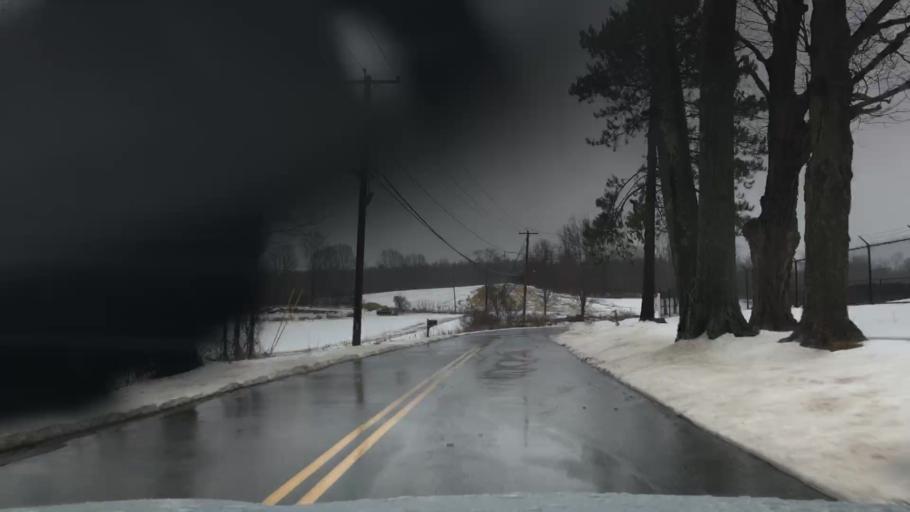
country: US
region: Massachusetts
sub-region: Hampshire County
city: Belchertown
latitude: 42.2831
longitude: -72.4261
